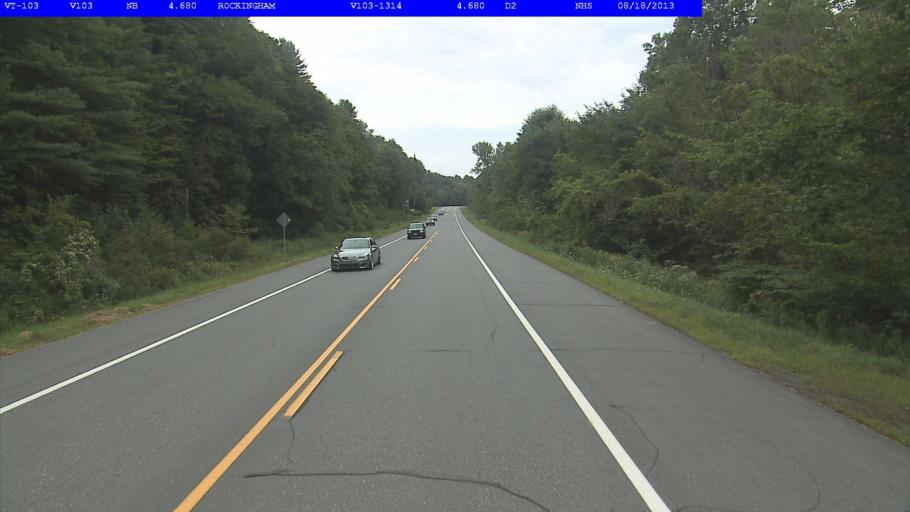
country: US
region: Vermont
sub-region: Windham County
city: Rockingham
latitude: 43.2091
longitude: -72.5376
